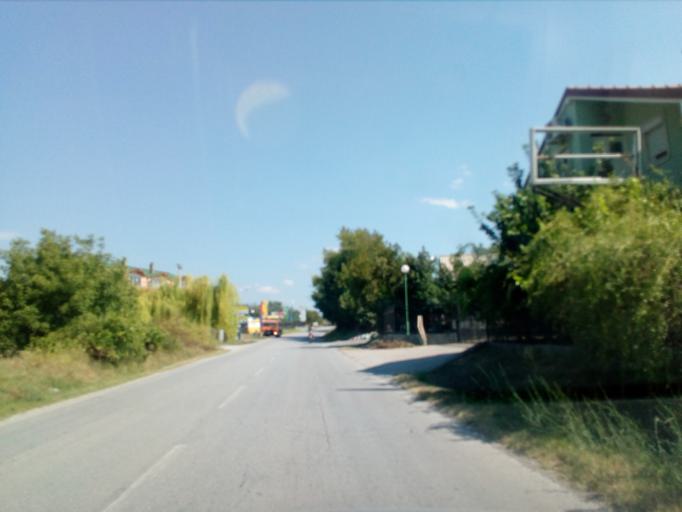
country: MK
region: Veles
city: Veles
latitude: 41.7324
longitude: 21.7780
